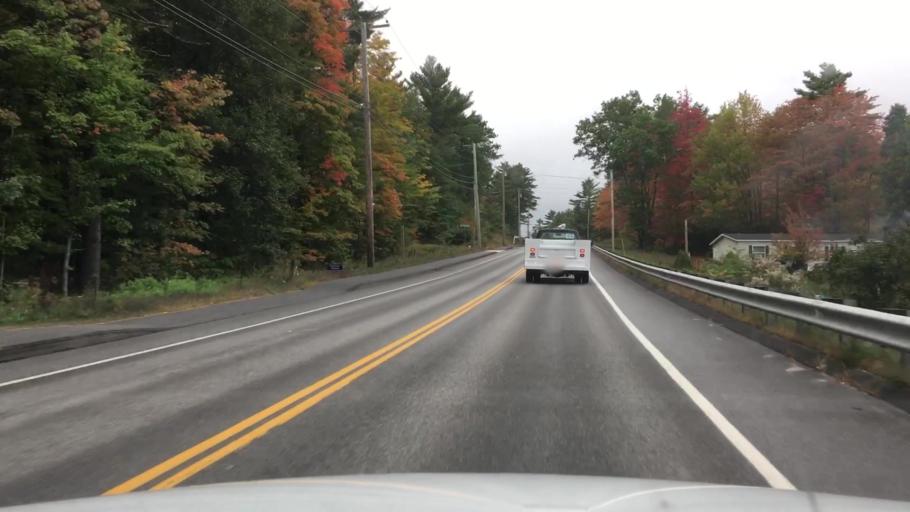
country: US
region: Maine
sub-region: Androscoggin County
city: Poland
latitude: 44.0651
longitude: -70.3990
